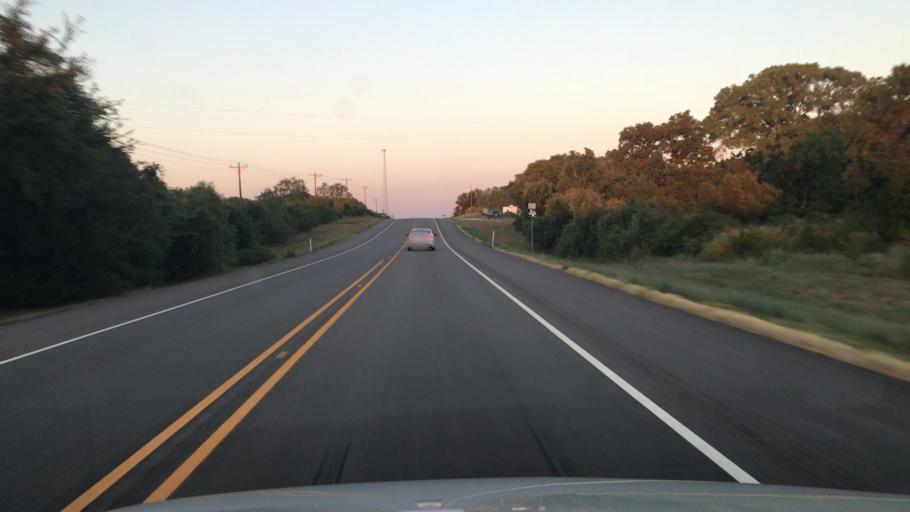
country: US
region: Texas
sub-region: Somervell County
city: Glen Rose
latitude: 32.1923
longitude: -97.8433
